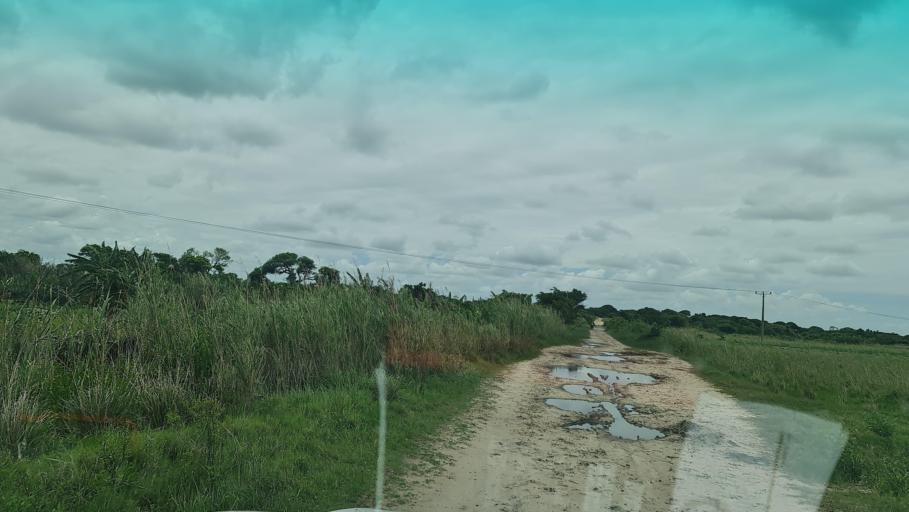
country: MZ
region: Maputo City
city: Maputo
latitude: -25.7012
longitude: 32.7048
